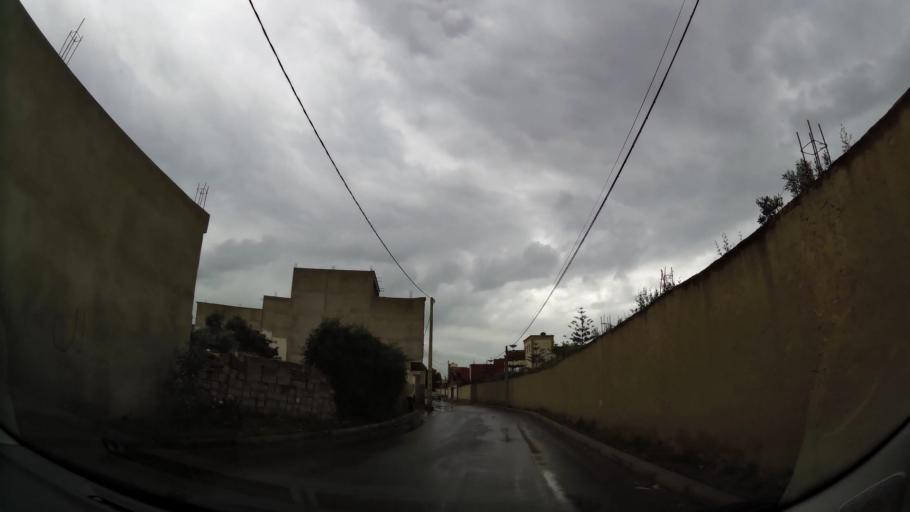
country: MA
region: Oriental
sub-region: Nador
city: Nador
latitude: 35.1491
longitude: -2.9881
